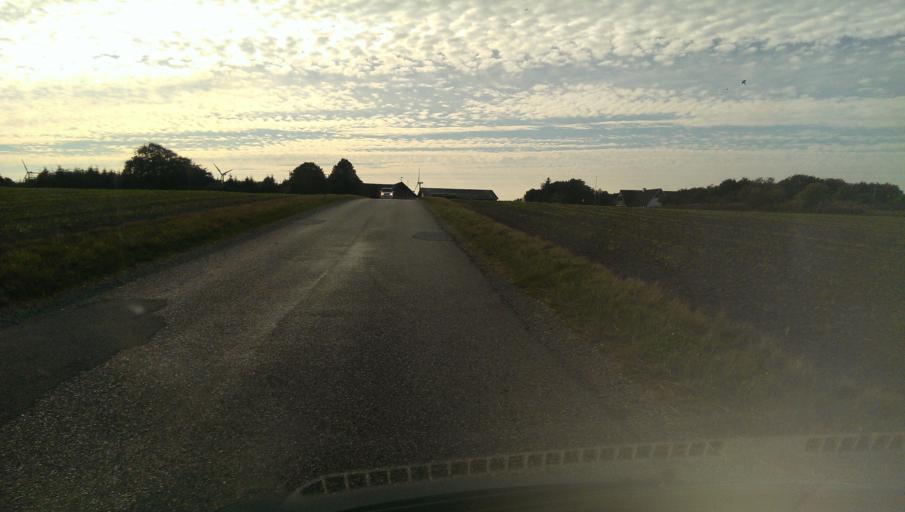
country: DK
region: South Denmark
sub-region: Esbjerg Kommune
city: Tjaereborg
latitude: 55.4780
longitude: 8.5593
